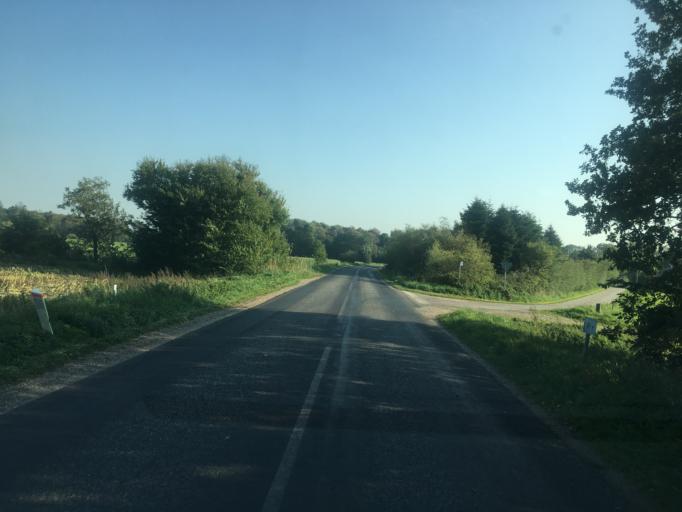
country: DE
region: Schleswig-Holstein
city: Bramstedtlund
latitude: 54.9605
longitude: 9.0520
